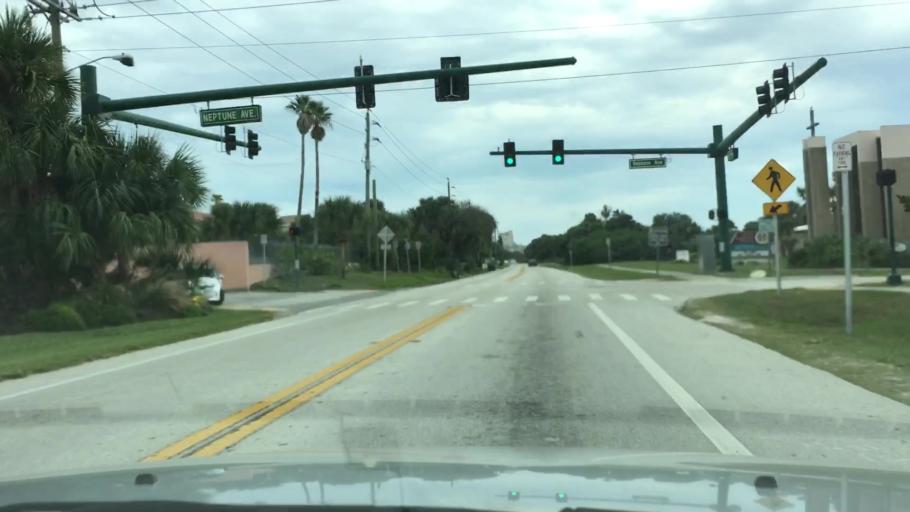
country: US
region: Florida
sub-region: Volusia County
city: Ormond Beach
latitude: 29.3014
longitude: -81.0447
